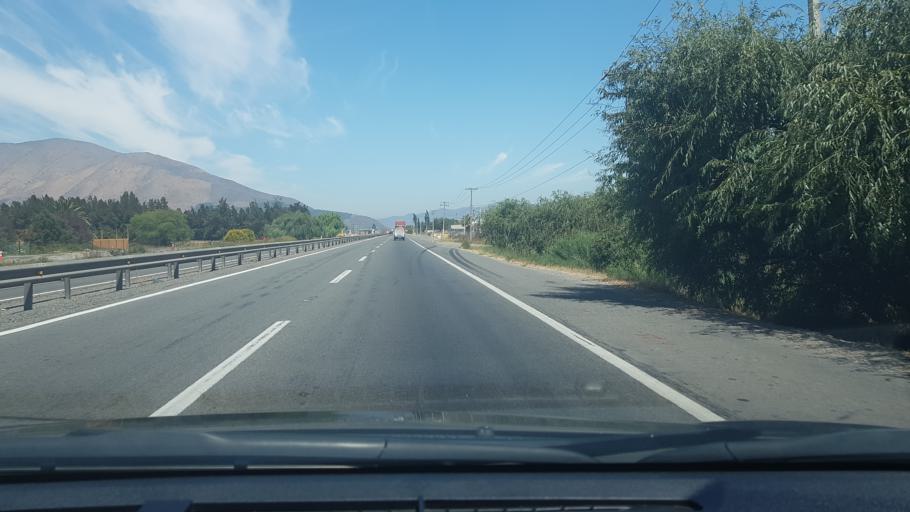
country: CL
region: Valparaiso
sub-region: Provincia de San Felipe
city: Llaillay
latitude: -32.8498
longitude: -70.9505
